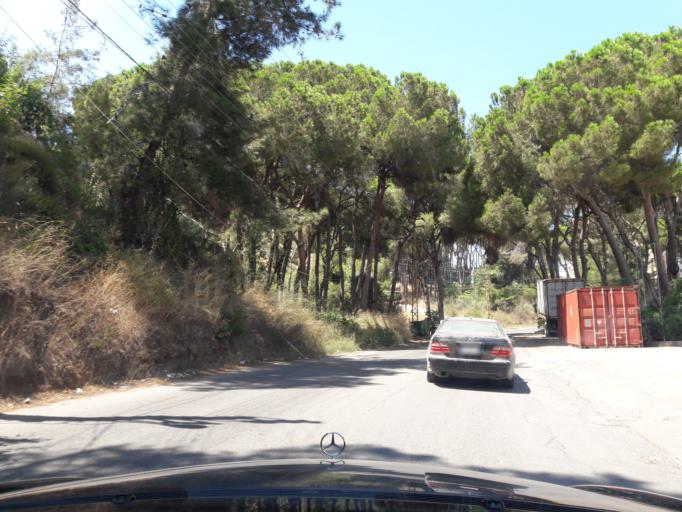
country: LB
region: Mont-Liban
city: Djounie
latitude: 33.9250
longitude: 35.6603
